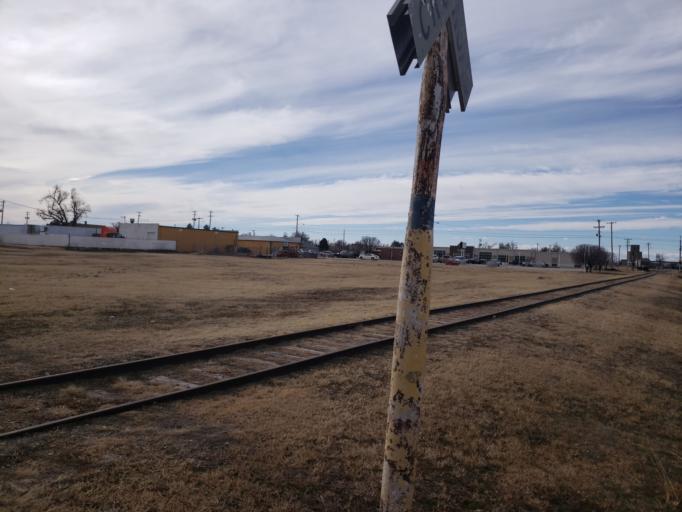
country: US
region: Kansas
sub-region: Ford County
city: Dodge City
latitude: 37.7421
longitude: -100.0177
